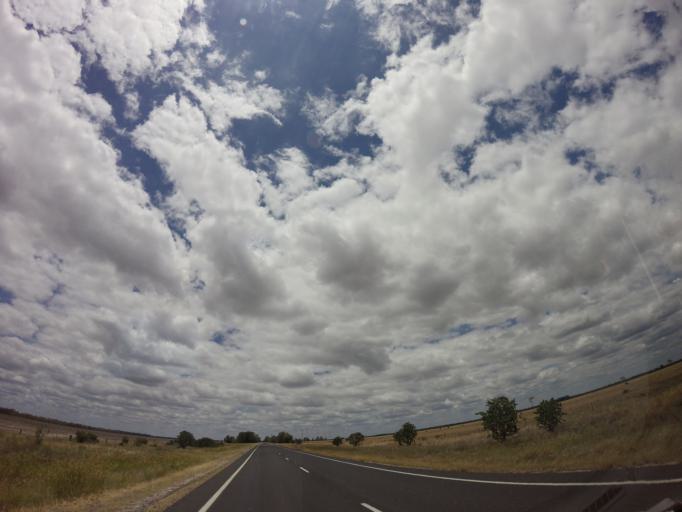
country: AU
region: Queensland
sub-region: Goondiwindi
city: Goondiwindi
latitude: -28.1717
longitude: 150.5016
